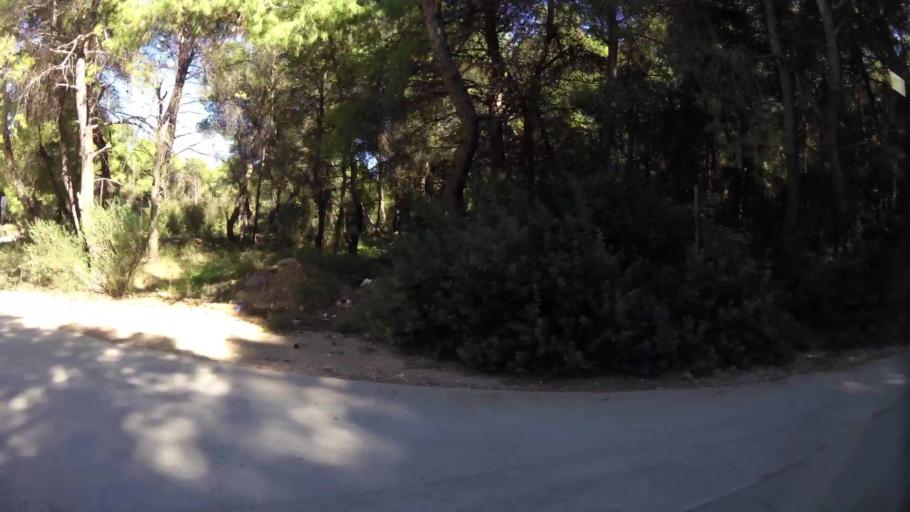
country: GR
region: Attica
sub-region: Nomarchia Athinas
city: Ekali
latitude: 38.1104
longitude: 23.8259
